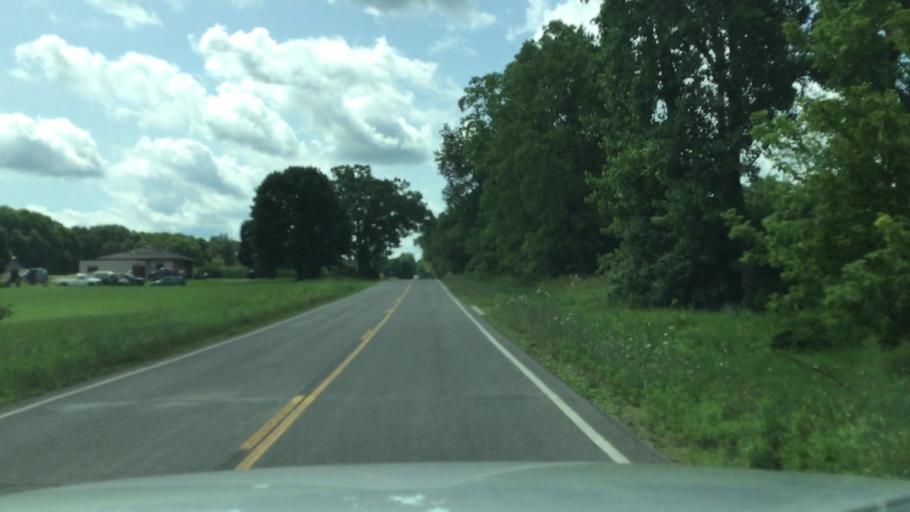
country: US
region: Michigan
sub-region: Montcalm County
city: Greenville
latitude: 43.1538
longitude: -85.2136
